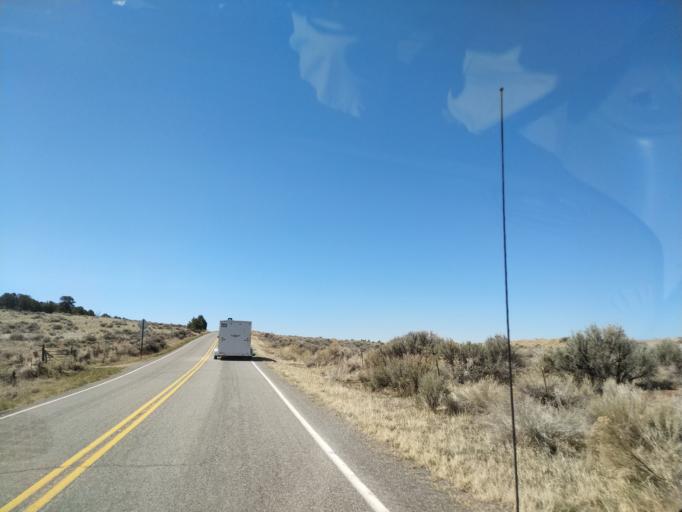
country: US
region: Colorado
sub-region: Mesa County
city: Redlands
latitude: 39.0043
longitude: -108.7053
